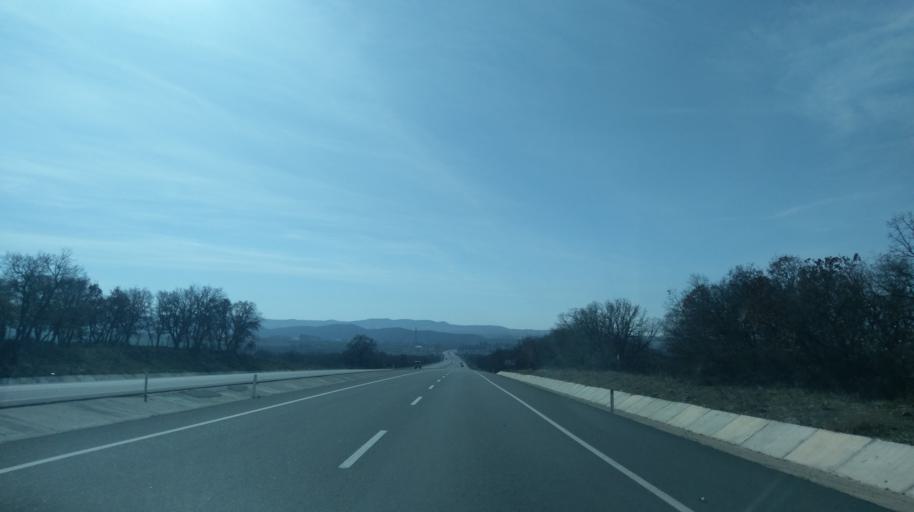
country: TR
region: Edirne
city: Kesan
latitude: 40.8969
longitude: 26.6330
